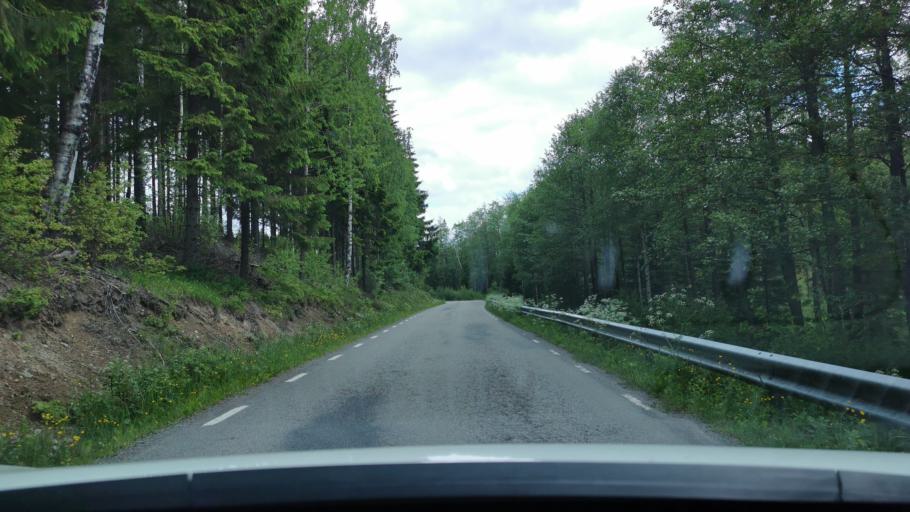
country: SE
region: Vaestra Goetaland
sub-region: Bengtsfors Kommun
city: Dals Langed
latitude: 58.8184
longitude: 12.3273
